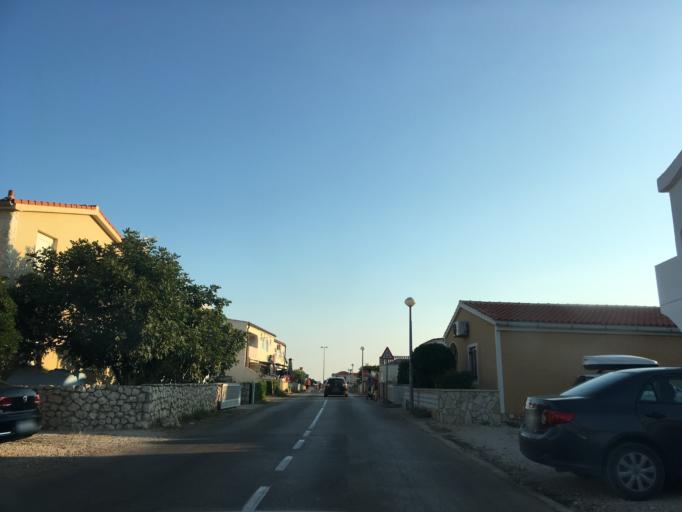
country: HR
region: Zadarska
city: Vir
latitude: 44.2963
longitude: 15.1171
